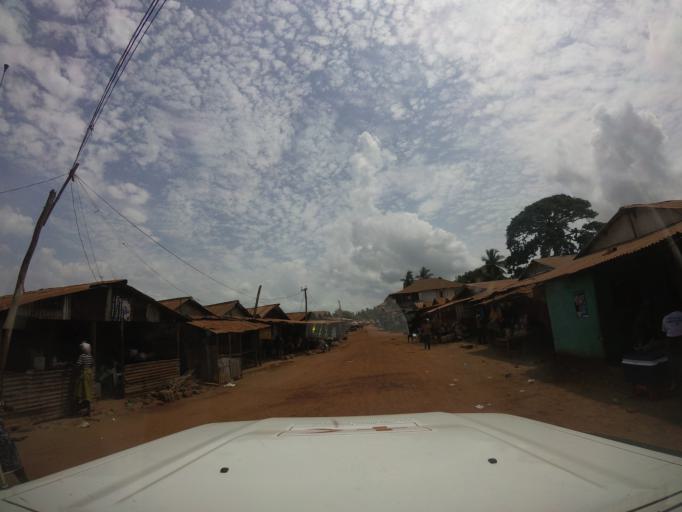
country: LR
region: Grand Cape Mount
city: Robertsport
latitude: 6.7554
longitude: -11.3619
